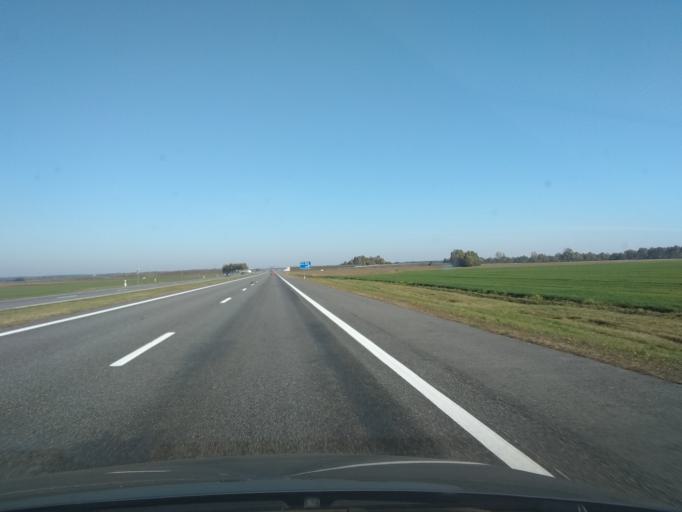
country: BY
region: Brest
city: Antopal'
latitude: 52.3011
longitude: 24.5881
